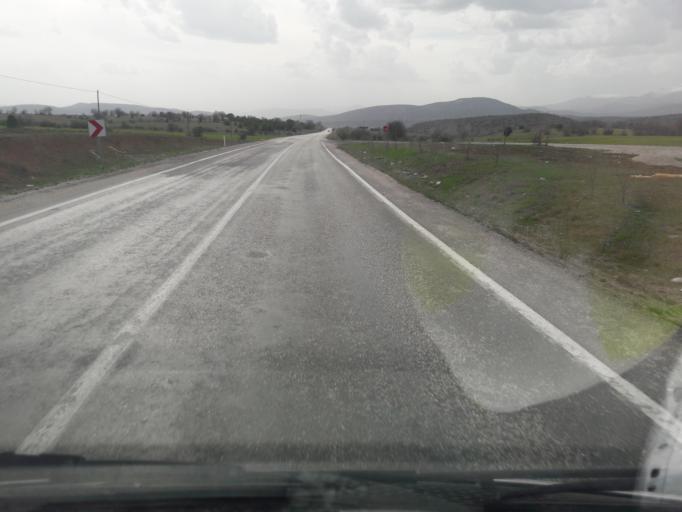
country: TR
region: Gumushane
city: Evren
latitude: 40.1699
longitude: 39.2525
